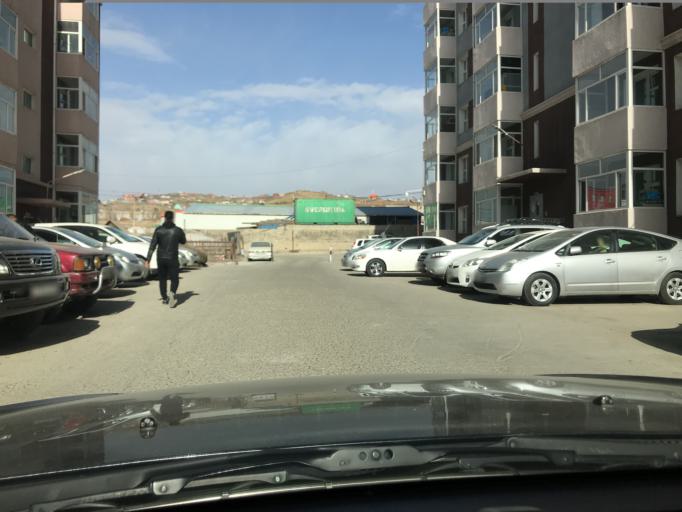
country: MN
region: Ulaanbaatar
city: Ulaanbaatar
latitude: 47.9226
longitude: 106.9550
